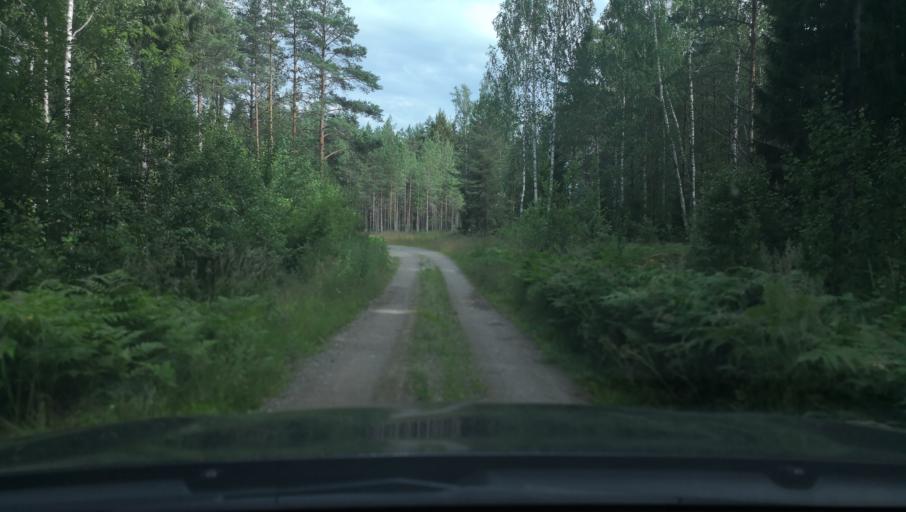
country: SE
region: Vaestmanland
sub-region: Surahammars Kommun
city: Surahammar
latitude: 59.6589
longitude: 16.0961
